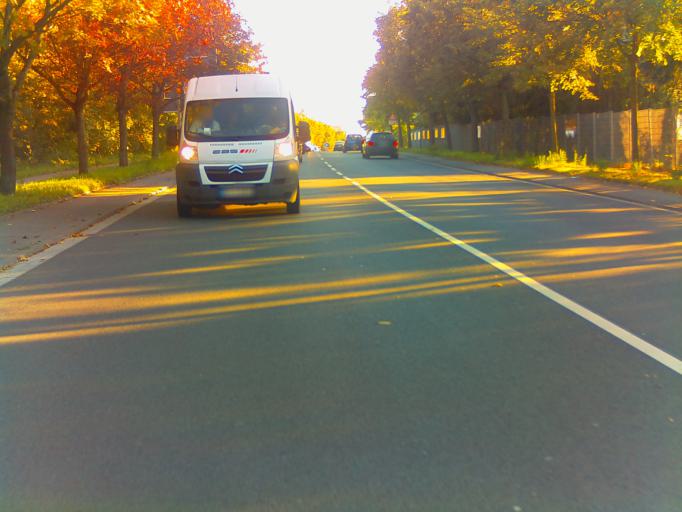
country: DE
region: Hesse
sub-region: Regierungsbezirk Darmstadt
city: Bensheim
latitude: 49.6945
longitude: 8.6103
